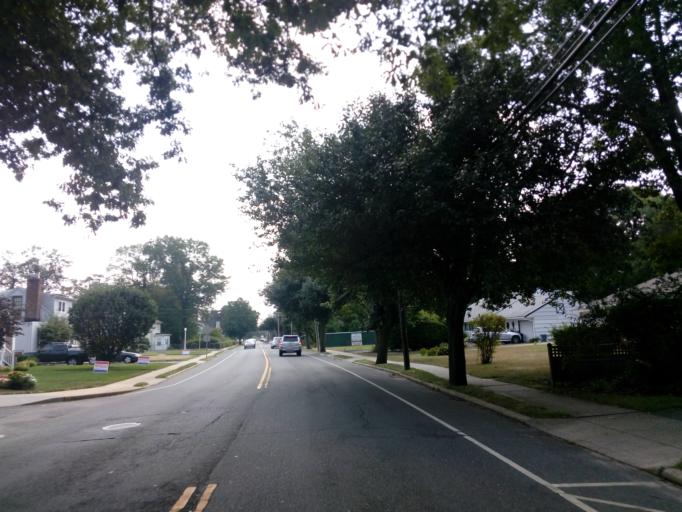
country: US
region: New York
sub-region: Nassau County
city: Glen Cove
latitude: 40.8761
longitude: -73.6307
